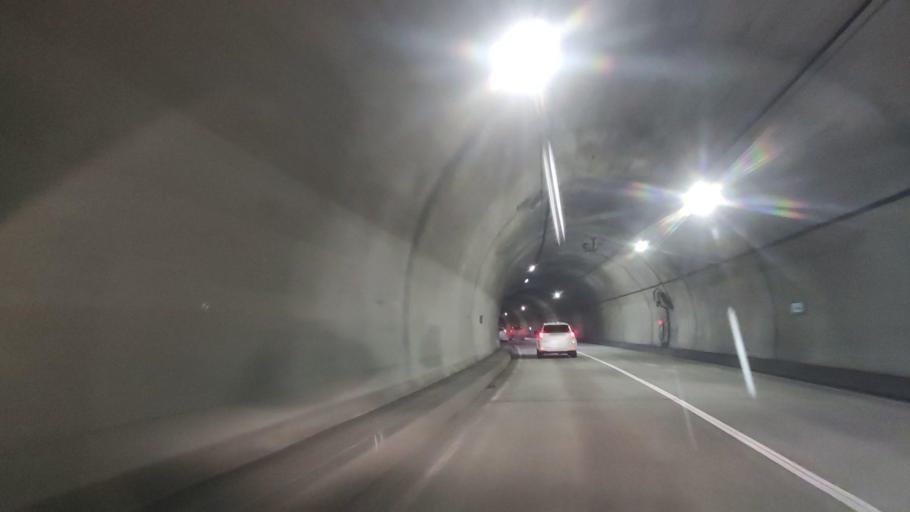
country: JP
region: Hokkaido
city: Ishikari
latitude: 43.5394
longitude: 141.3927
